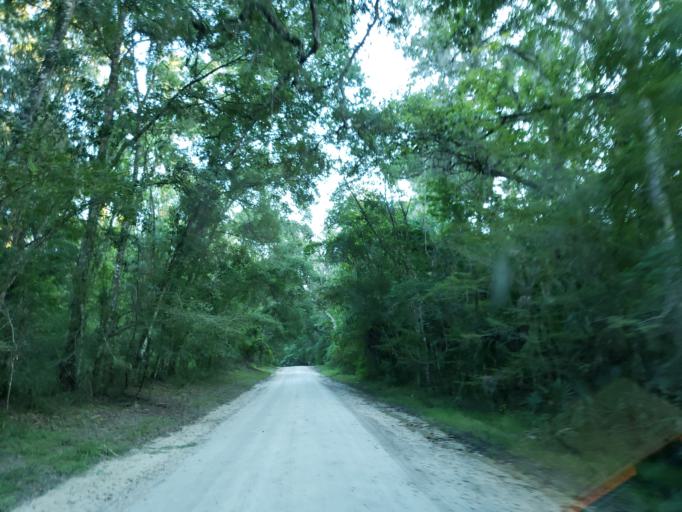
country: US
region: Florida
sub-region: Alachua County
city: Gainesville
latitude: 29.4861
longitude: -82.2770
